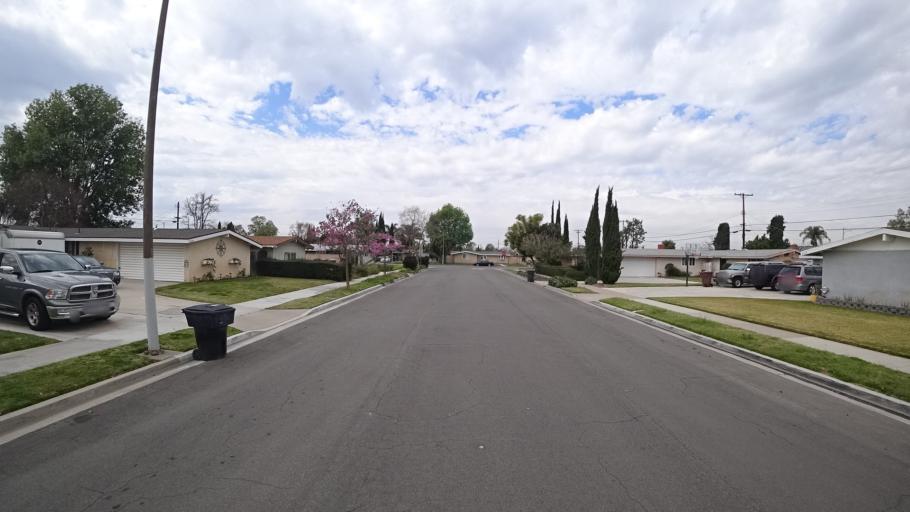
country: US
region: California
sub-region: Orange County
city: Anaheim
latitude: 33.8342
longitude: -117.8875
